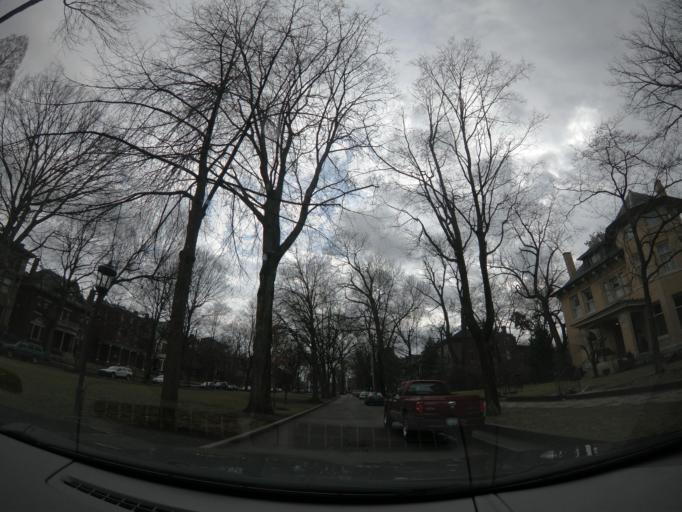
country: US
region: Kentucky
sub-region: Jefferson County
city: Louisville
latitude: 38.2292
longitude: -85.7637
